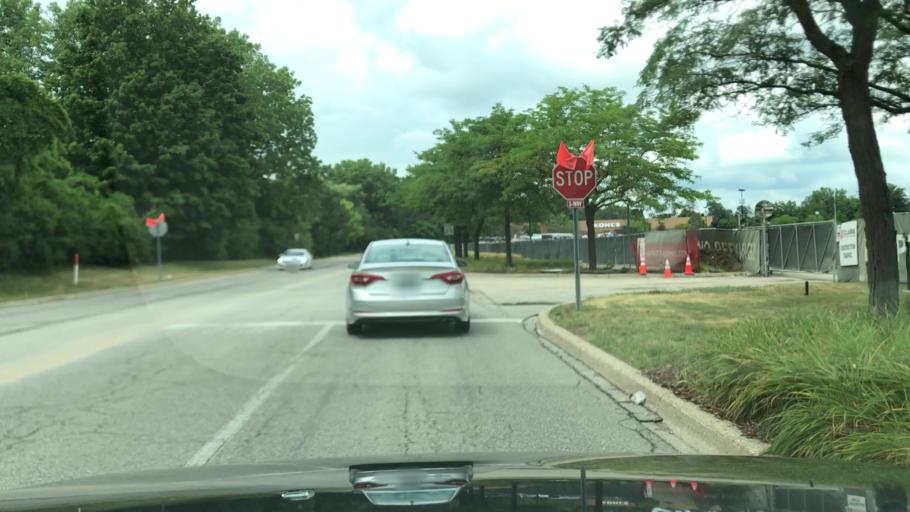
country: US
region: Michigan
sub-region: Kent County
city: East Grand Rapids
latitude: 42.9152
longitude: -85.5921
